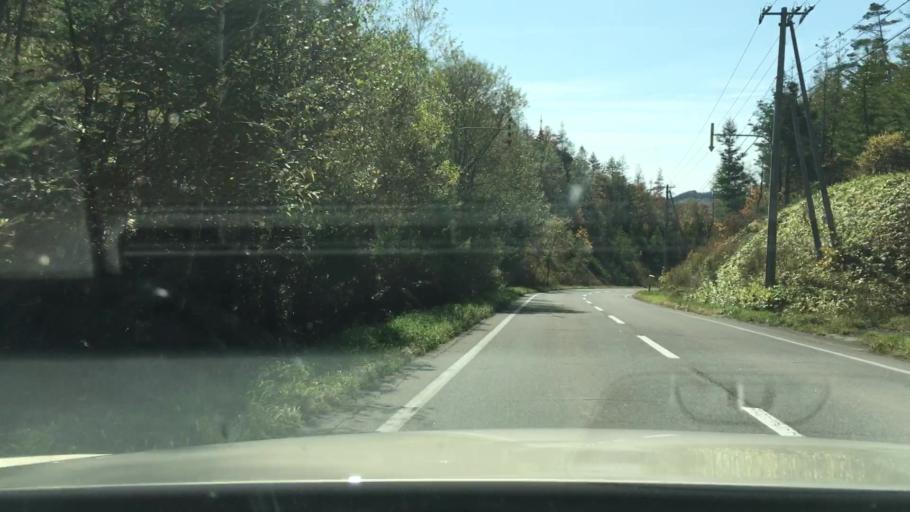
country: JP
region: Hokkaido
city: Kitami
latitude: 43.5969
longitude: 143.6820
